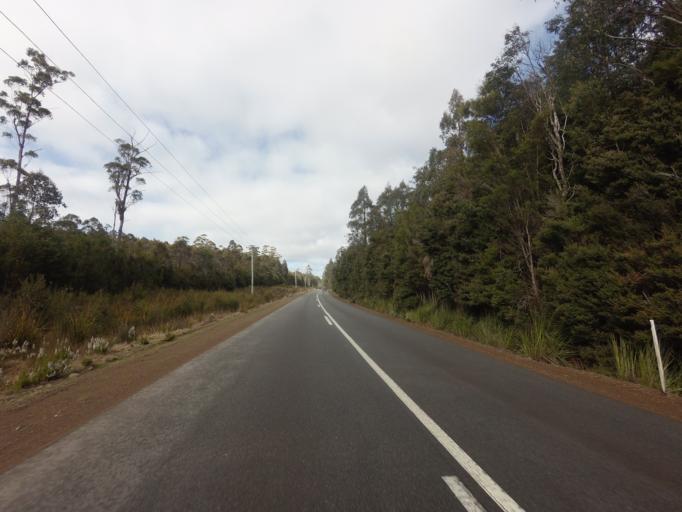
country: AU
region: Tasmania
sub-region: Huon Valley
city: Geeveston
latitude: -43.3668
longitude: 146.9589
